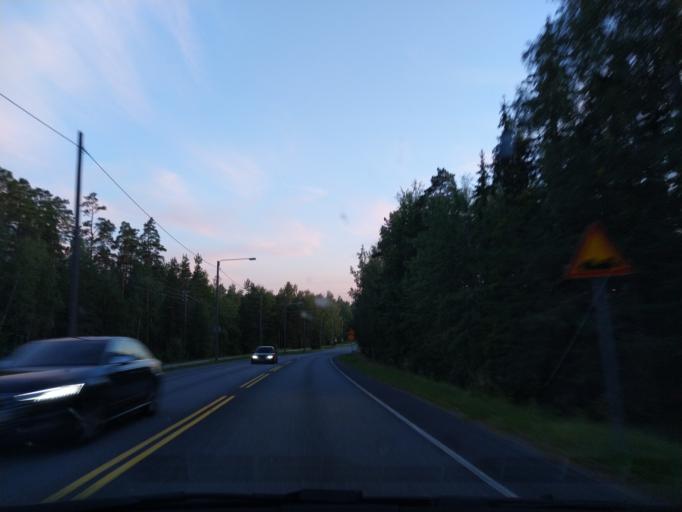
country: FI
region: Uusimaa
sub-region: Helsinki
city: Tuusula
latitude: 60.3496
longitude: 25.0061
